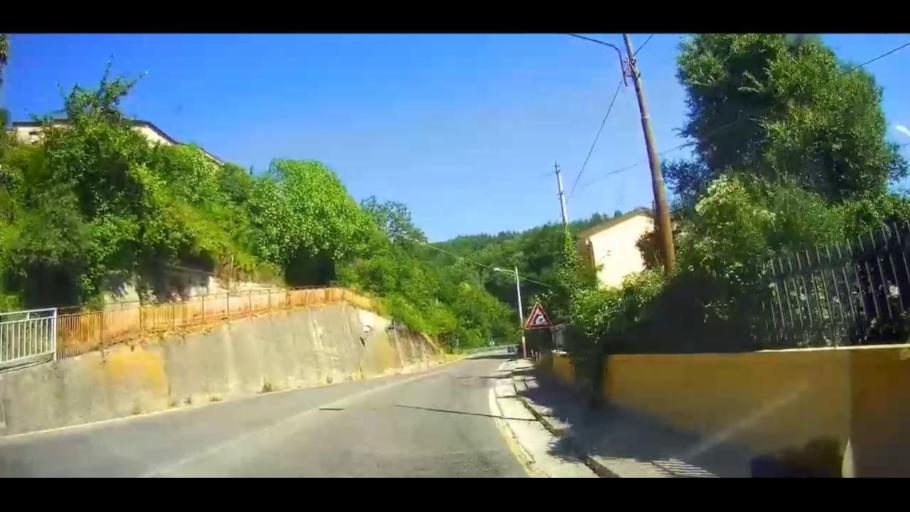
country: IT
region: Calabria
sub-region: Provincia di Cosenza
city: Celico
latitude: 39.3109
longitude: 16.3395
